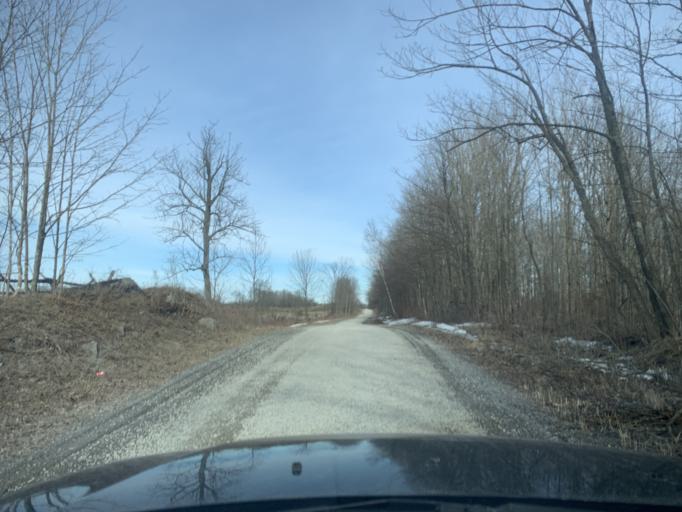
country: CA
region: Ontario
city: Deseronto
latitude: 44.3942
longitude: -77.1568
